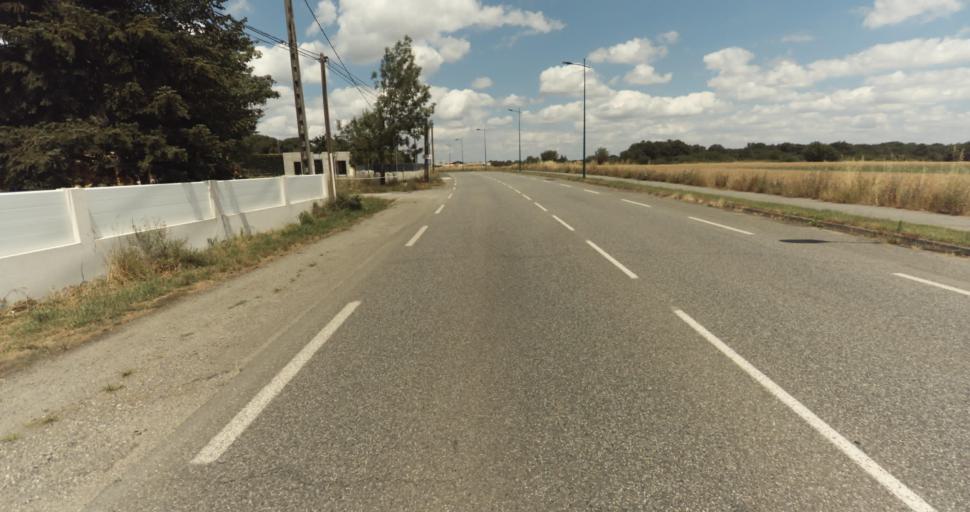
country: FR
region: Midi-Pyrenees
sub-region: Departement de la Haute-Garonne
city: Fontenilles
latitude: 43.5423
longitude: 1.1902
